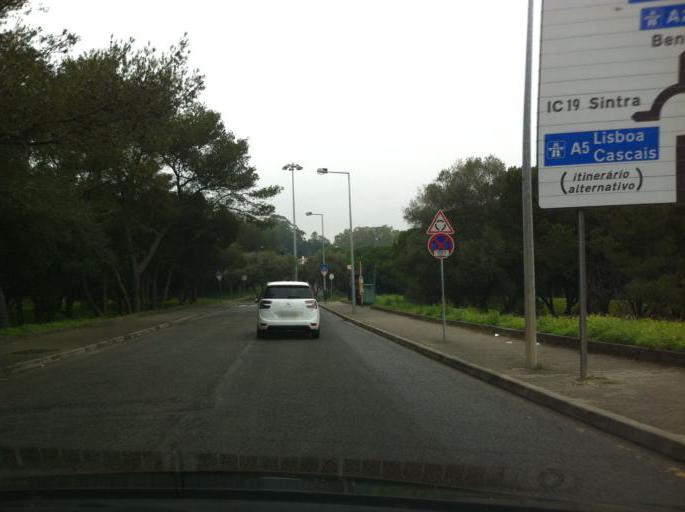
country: PT
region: Lisbon
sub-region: Oeiras
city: Alges
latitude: 38.7130
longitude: -9.2008
